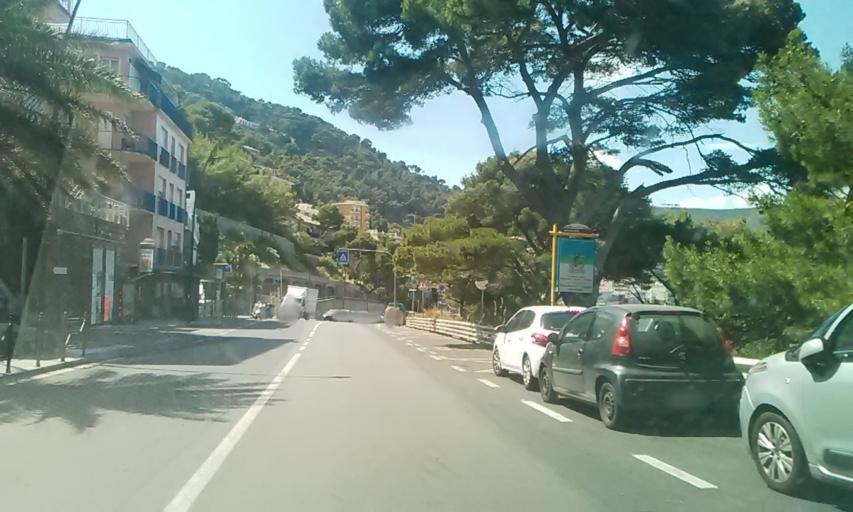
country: IT
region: Liguria
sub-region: Provincia di Savona
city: Laigueglia
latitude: 43.9686
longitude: 8.1629
